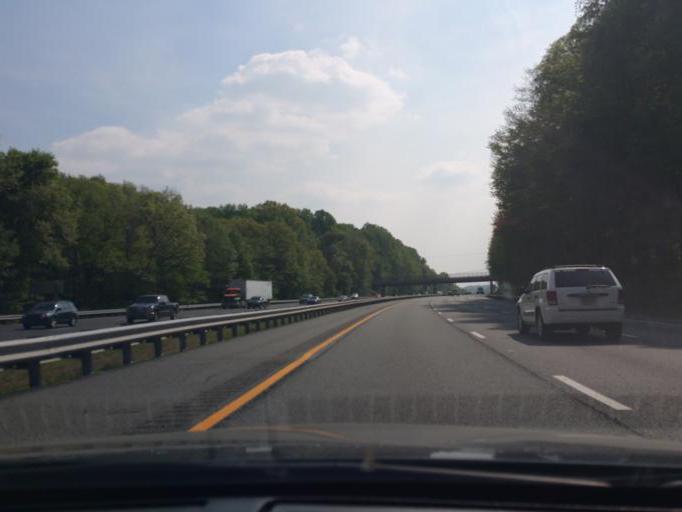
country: US
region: Maryland
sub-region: Harford County
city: Havre de Grace
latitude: 39.5640
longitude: -76.1442
